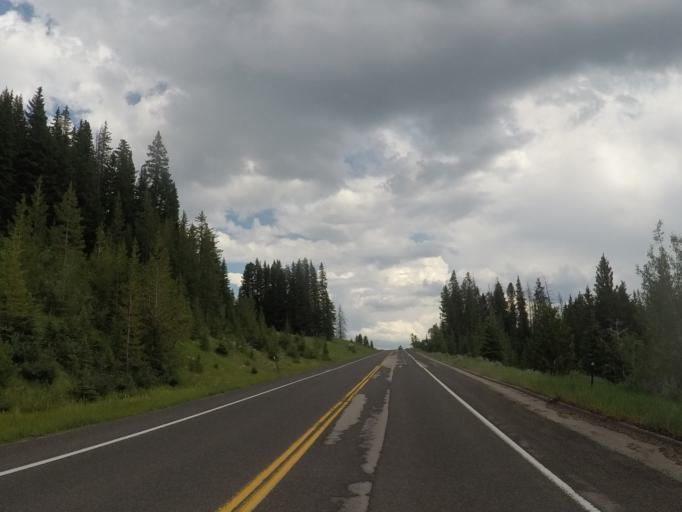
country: US
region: Montana
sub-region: Carbon County
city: Red Lodge
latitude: 44.9260
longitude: -109.6369
